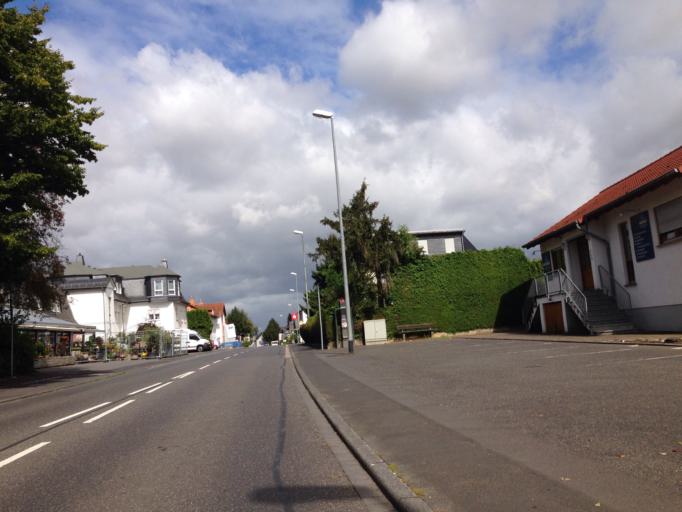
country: DE
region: Hesse
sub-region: Regierungsbezirk Giessen
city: Elz
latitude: 50.4111
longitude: 8.0615
